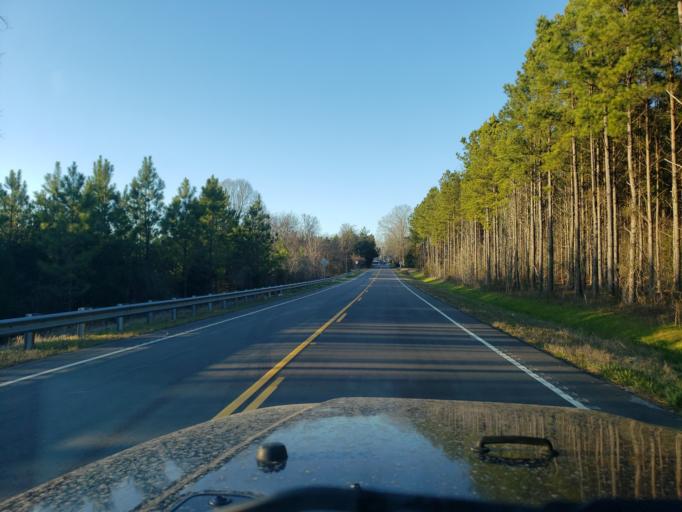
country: US
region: South Carolina
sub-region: Cherokee County
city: Blacksburg
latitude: 35.0394
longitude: -81.4043
